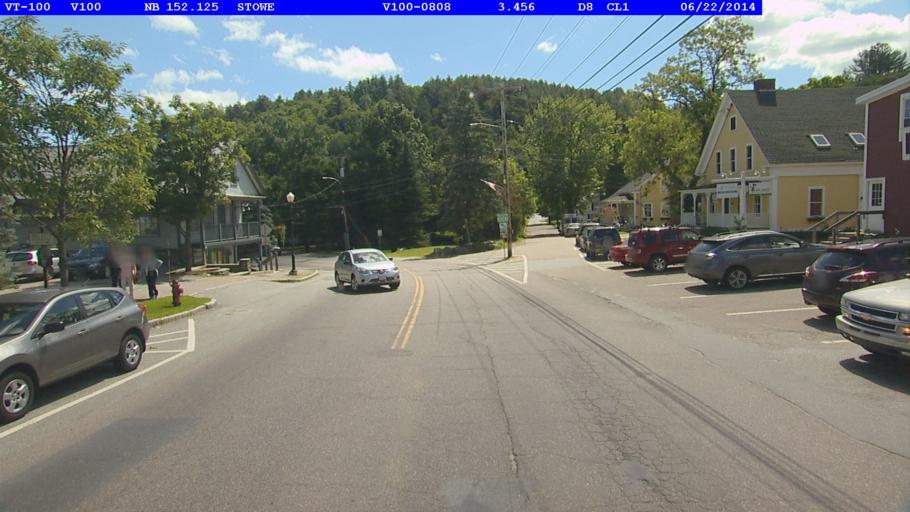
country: US
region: Vermont
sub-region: Lamoille County
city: Morristown
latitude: 44.4653
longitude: -72.6848
